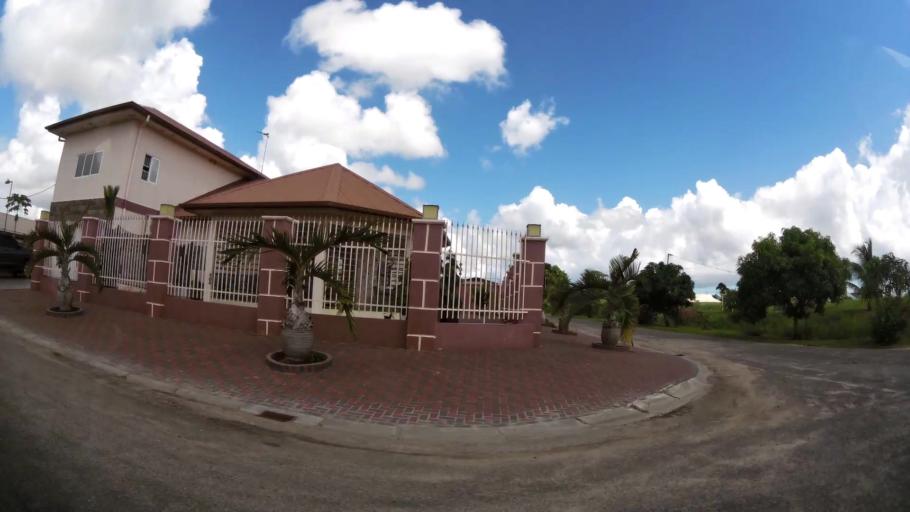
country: SR
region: Paramaribo
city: Paramaribo
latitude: 5.8660
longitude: -55.1322
